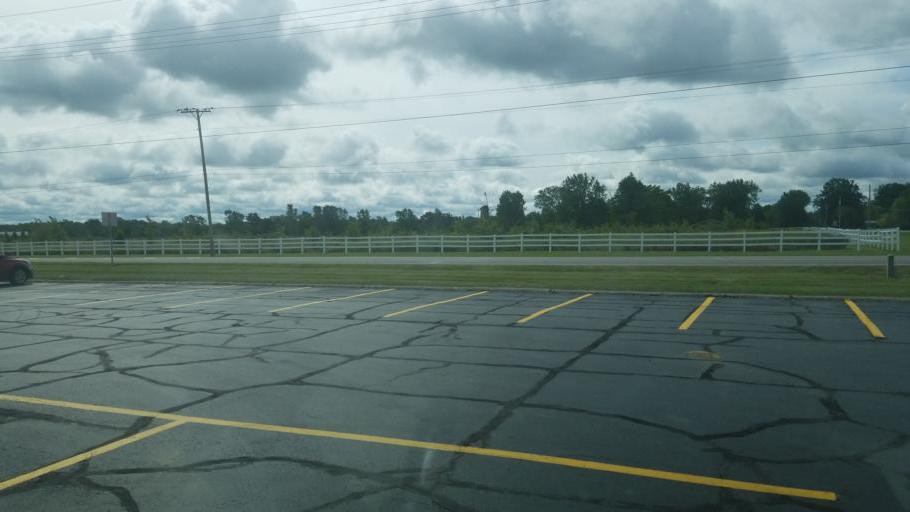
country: US
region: Ohio
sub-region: Lorain County
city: Oberlin
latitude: 41.3093
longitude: -82.2165
